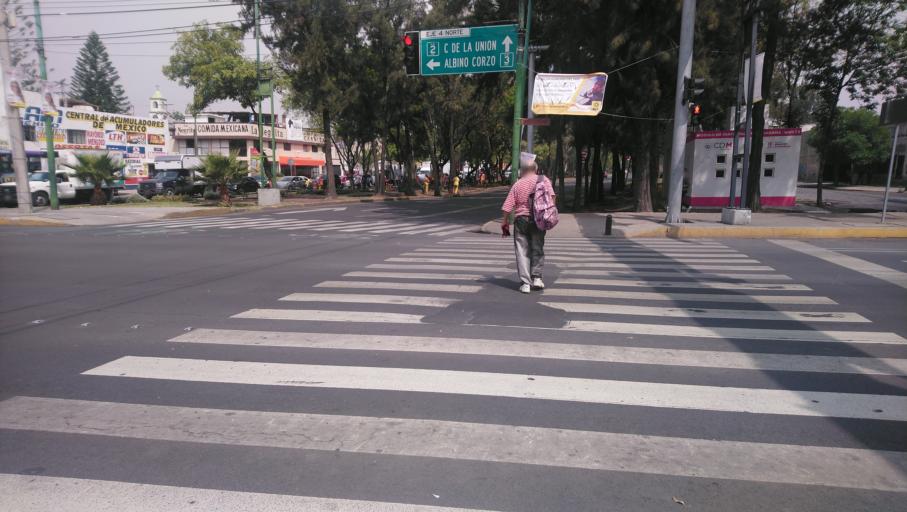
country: MX
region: Mexico City
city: Gustavo A. Madero
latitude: 19.4707
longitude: -99.1016
